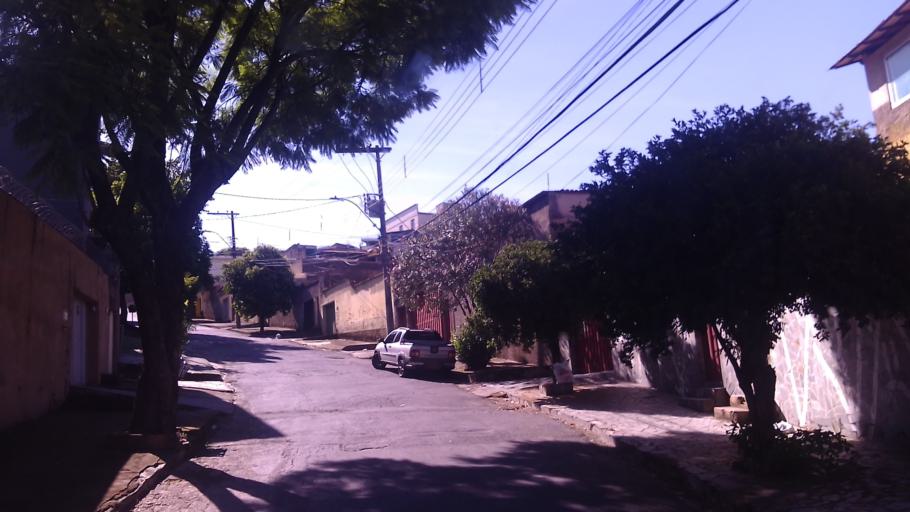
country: BR
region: Minas Gerais
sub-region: Contagem
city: Contagem
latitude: -19.9191
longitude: -44.0031
